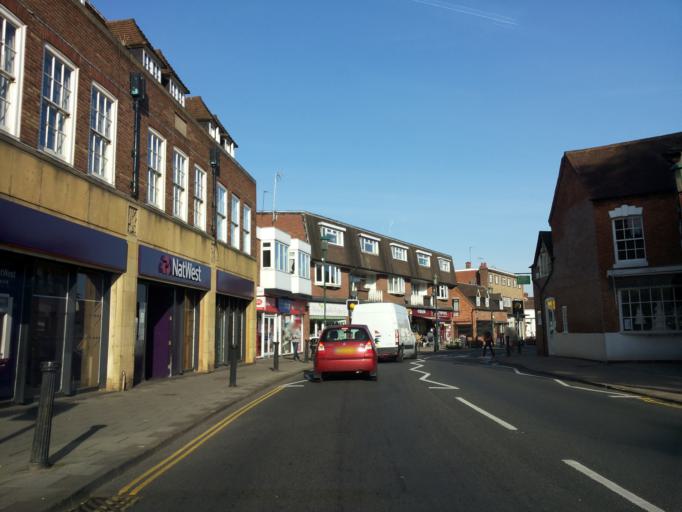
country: GB
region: England
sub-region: Solihull
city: Knowle
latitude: 52.3880
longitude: -1.7340
